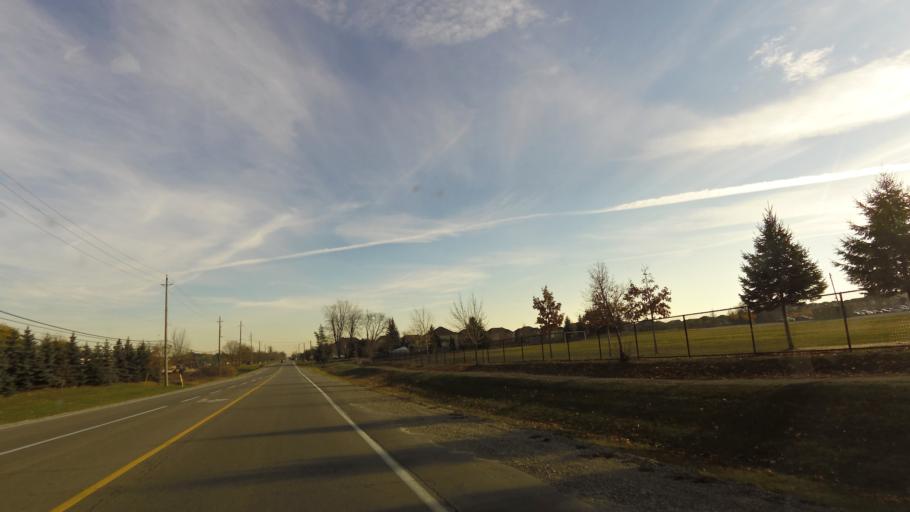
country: CA
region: Ontario
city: Brampton
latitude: 43.7858
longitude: -79.7287
